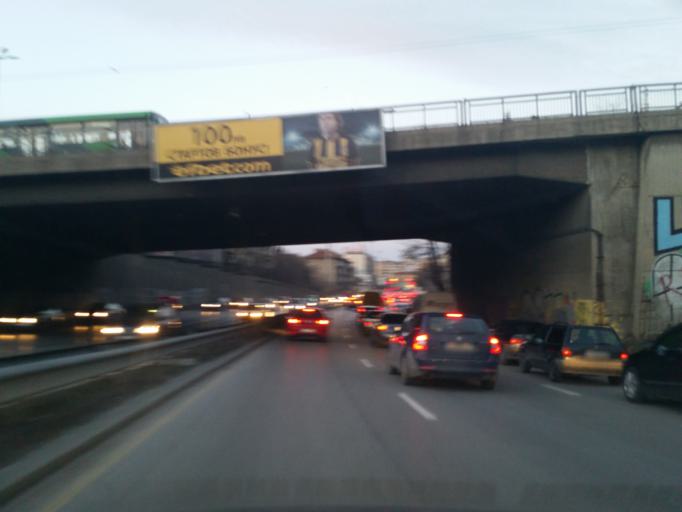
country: BG
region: Sofia-Capital
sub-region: Stolichna Obshtina
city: Sofia
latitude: 42.6830
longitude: 23.3473
